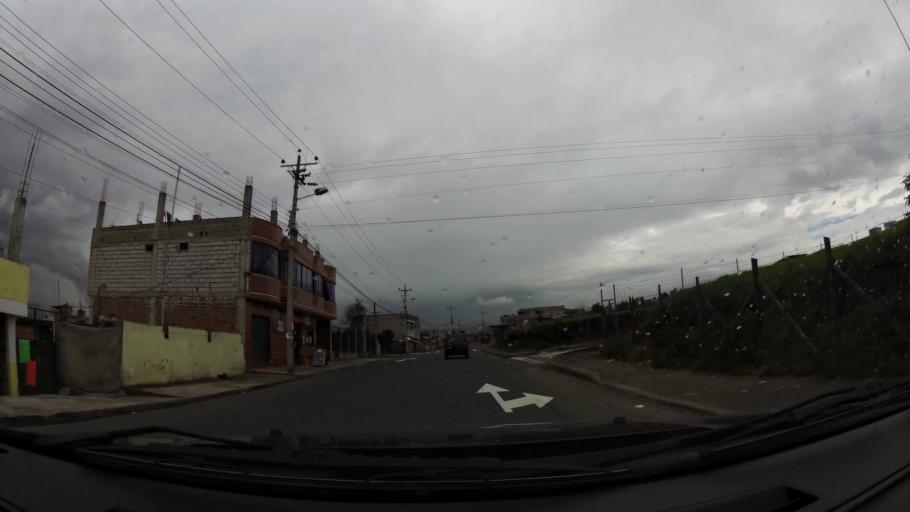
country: EC
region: Pichincha
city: Sangolqui
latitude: -0.3433
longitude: -78.5536
